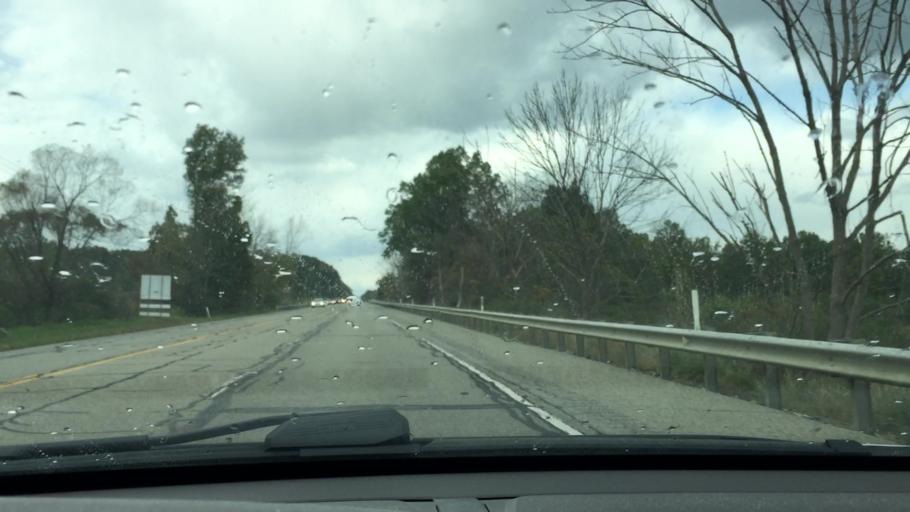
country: US
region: Pennsylvania
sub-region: Lawrence County
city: Oakwood
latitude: 41.0564
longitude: -80.4456
